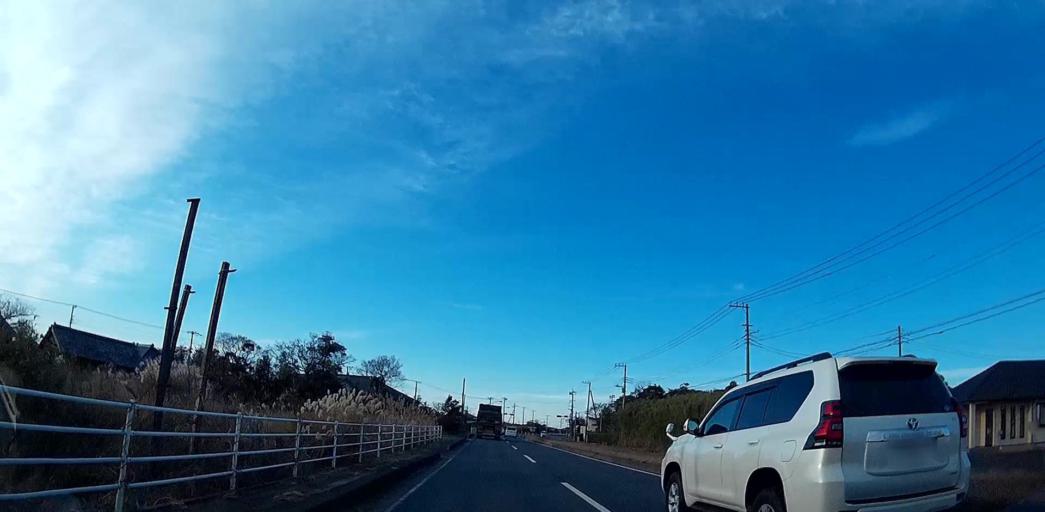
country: JP
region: Chiba
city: Omigawa
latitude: 35.8252
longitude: 140.7258
